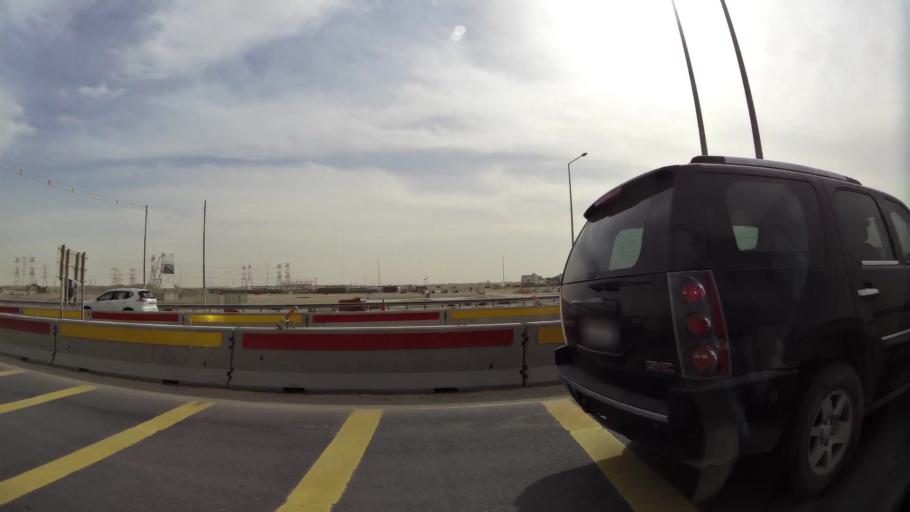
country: QA
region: Baladiyat ar Rayyan
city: Ash Shahaniyah
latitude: 25.3437
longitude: 51.3118
